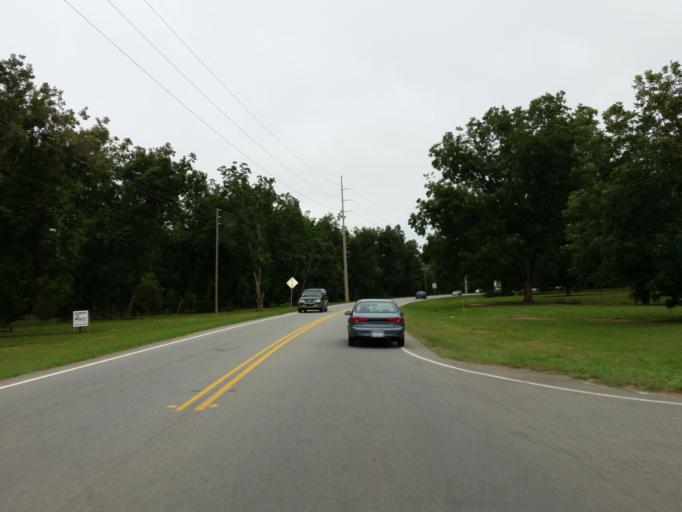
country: US
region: Georgia
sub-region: Peach County
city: Fort Valley
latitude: 32.5741
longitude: -83.8931
